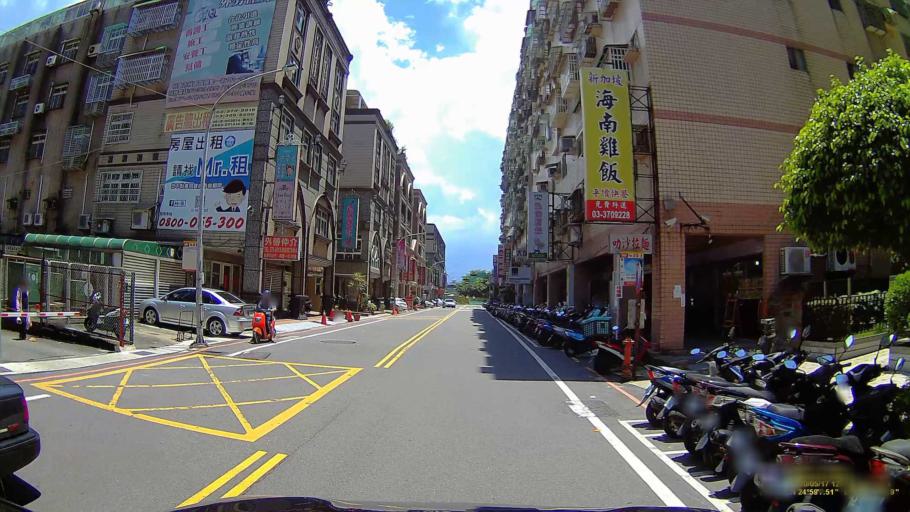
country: TW
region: Taiwan
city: Taoyuan City
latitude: 24.9853
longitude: 121.2885
